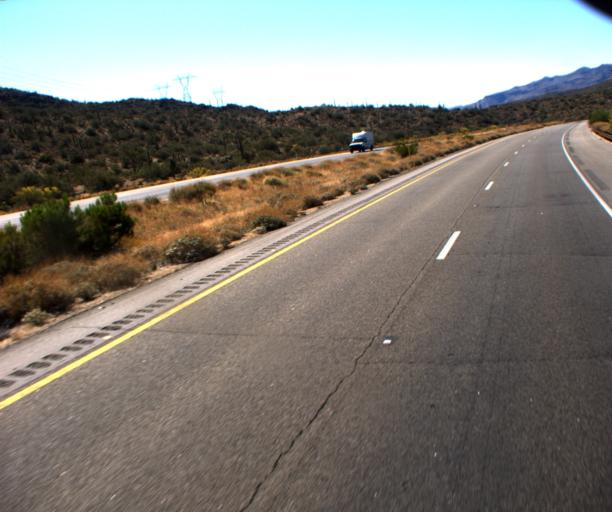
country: US
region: Arizona
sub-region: Yavapai County
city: Bagdad
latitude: 34.4162
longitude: -113.2337
